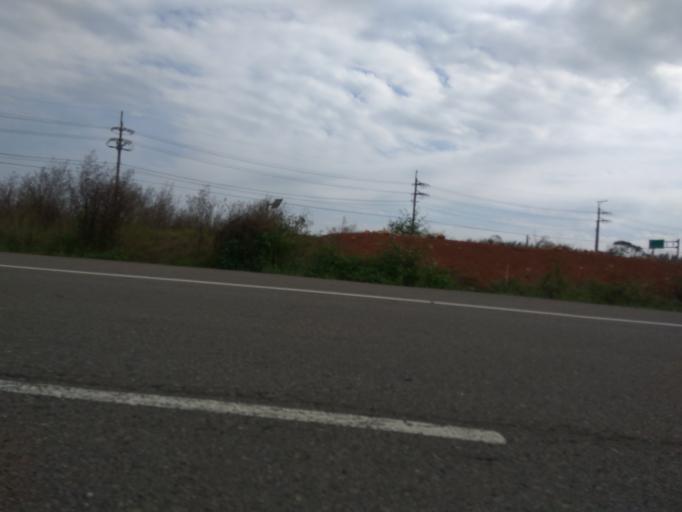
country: TW
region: Taiwan
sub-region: Hsinchu
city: Zhubei
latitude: 24.9733
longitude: 121.0266
